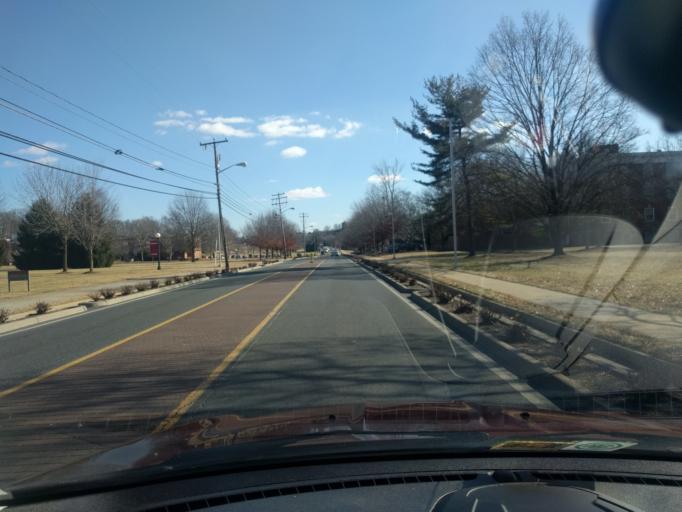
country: US
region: Virginia
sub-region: Rockingham County
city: Bridgewater
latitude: 38.3799
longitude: -78.9692
